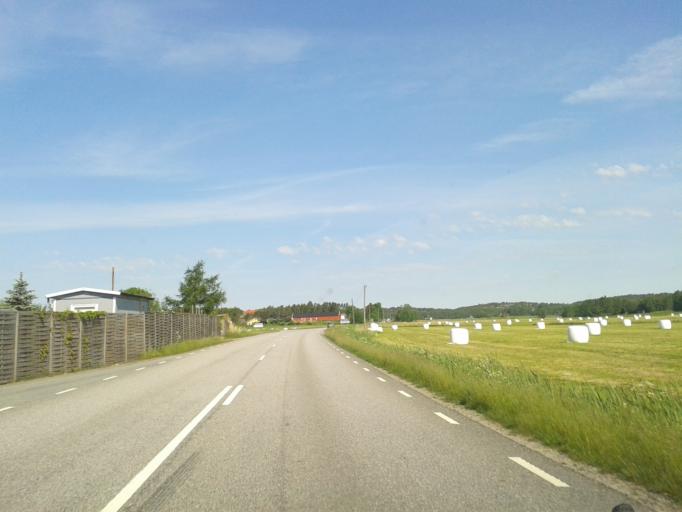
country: SE
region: Vaestra Goetaland
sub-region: Stromstads Kommun
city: Stroemstad
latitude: 58.8607
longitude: 11.2526
